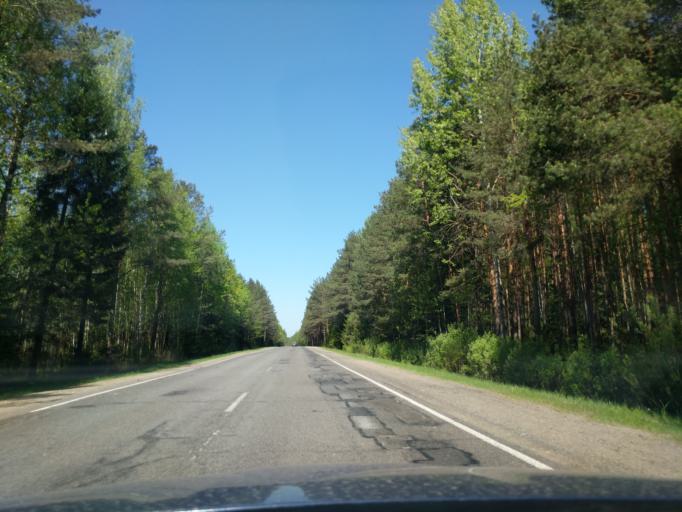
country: BY
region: Minsk
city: Il'ya
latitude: 54.4052
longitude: 27.3183
